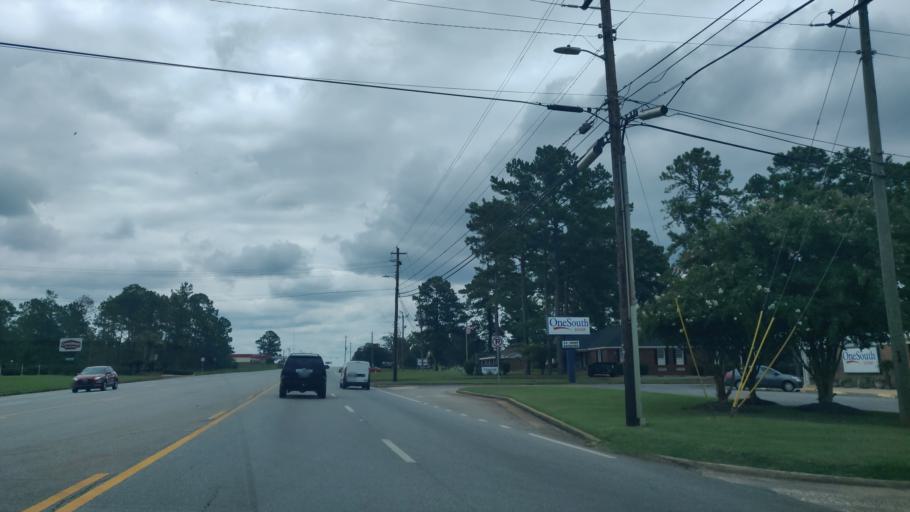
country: US
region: Georgia
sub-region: Terrell County
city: Dawson
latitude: 31.7615
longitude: -84.4375
